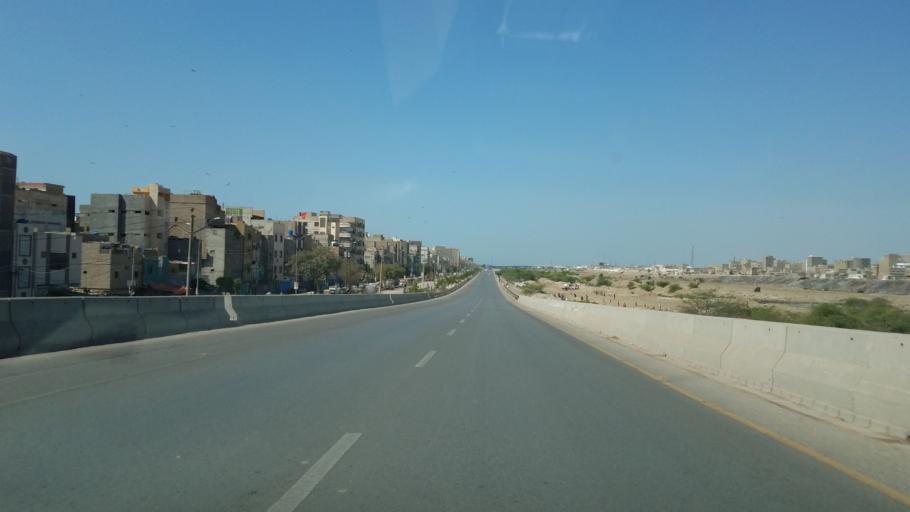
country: PK
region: Sindh
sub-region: Karachi District
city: Karachi
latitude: 24.8792
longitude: 66.9940
